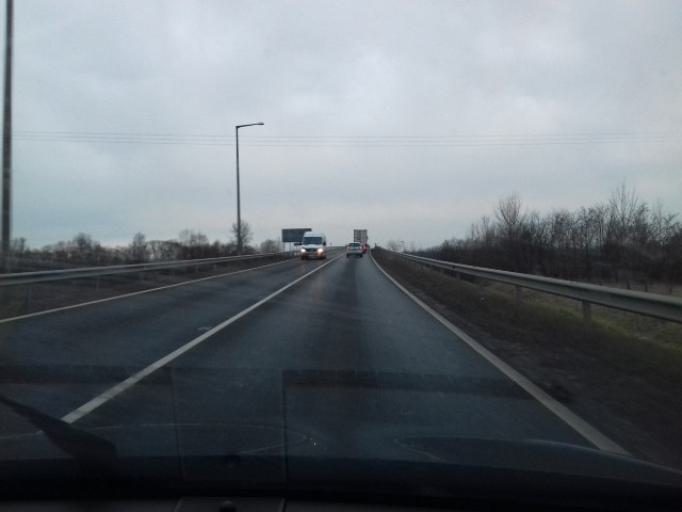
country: HU
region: Szabolcs-Szatmar-Bereg
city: Nyirpazony
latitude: 47.9491
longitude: 21.8207
